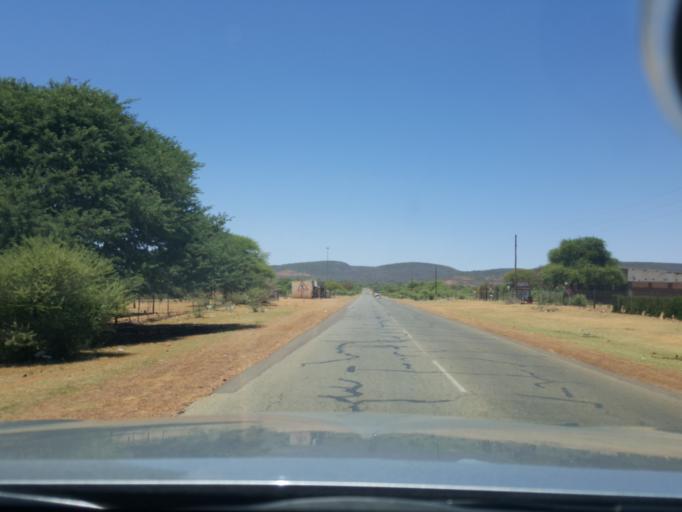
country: BW
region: South East
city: Lobatse
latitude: -25.2753
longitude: 25.9232
